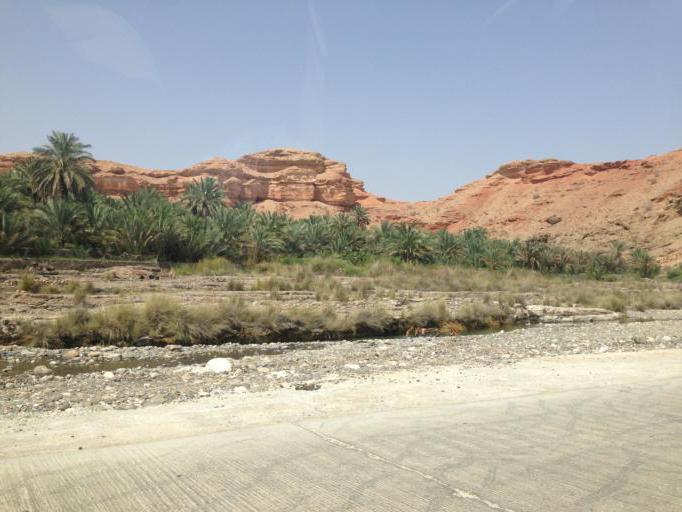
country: OM
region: Ash Sharqiyah
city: Ibra'
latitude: 23.0895
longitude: 58.8644
